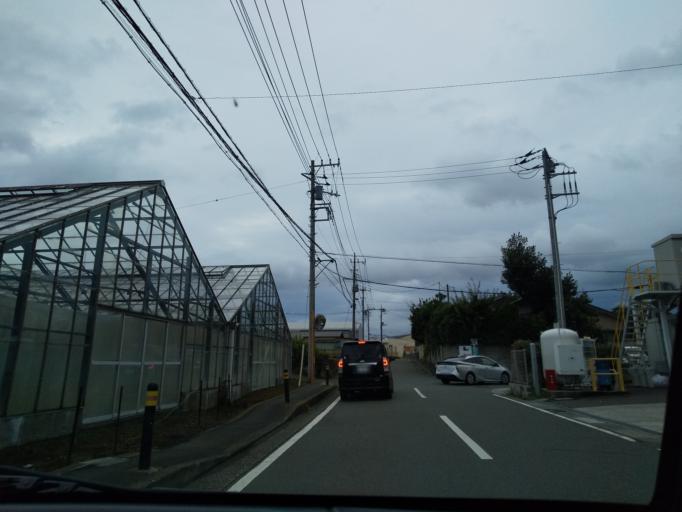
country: JP
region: Kanagawa
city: Minami-rinkan
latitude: 35.4389
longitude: 139.4391
